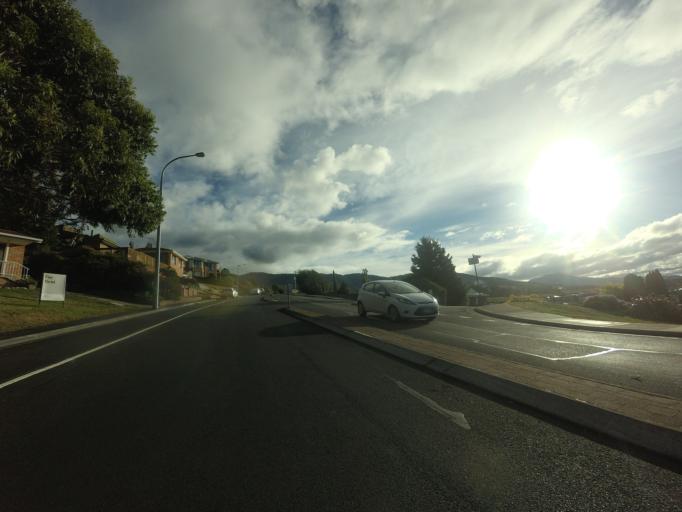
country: AU
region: Tasmania
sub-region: Glenorchy
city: Austins Ferry
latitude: -42.7736
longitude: 147.2437
